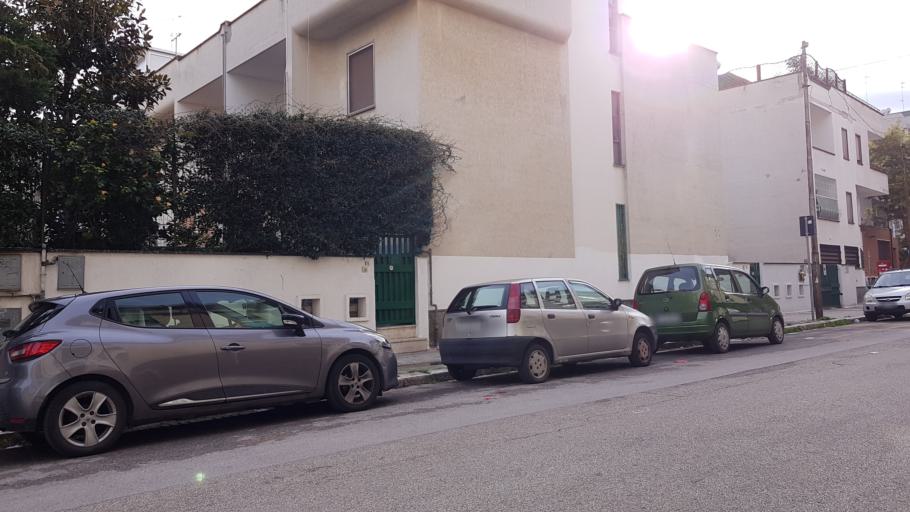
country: IT
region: Apulia
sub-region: Provincia di Brindisi
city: Brindisi
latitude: 40.6335
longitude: 17.9369
